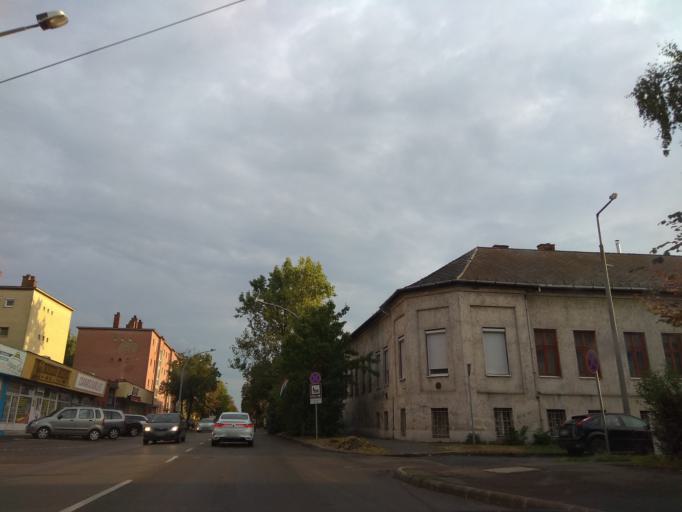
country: HU
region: Borsod-Abauj-Zemplen
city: Miskolc
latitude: 48.0986
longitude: 20.7976
